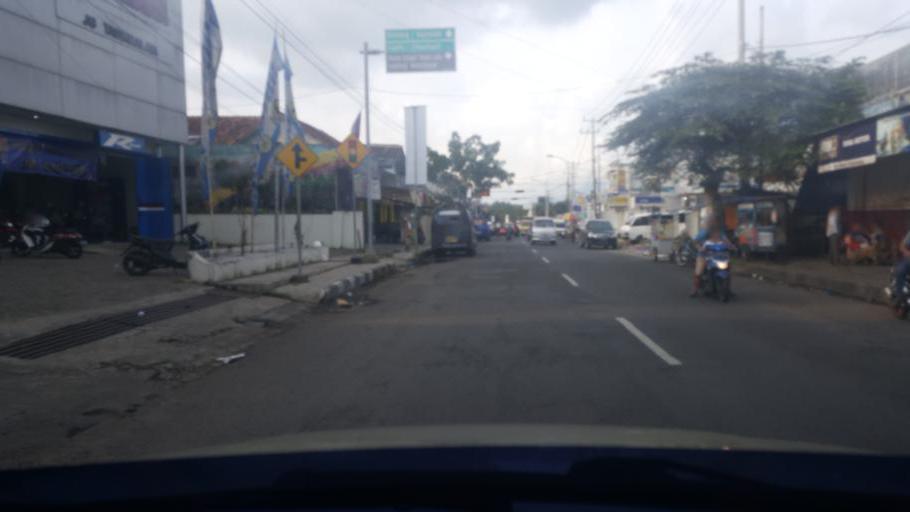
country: ID
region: West Java
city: Sindangpalay
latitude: -7.2888
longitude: 108.2004
